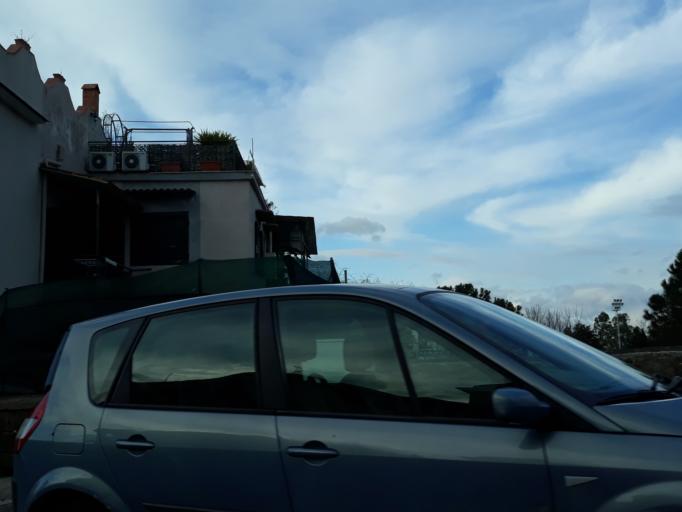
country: IT
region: Campania
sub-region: Provincia di Napoli
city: Mugnano di Napoli
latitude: 40.8843
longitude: 14.2299
